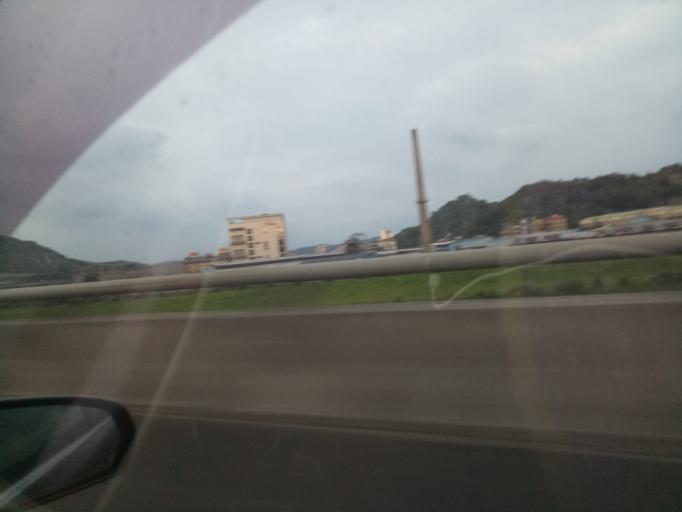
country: TW
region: Taiwan
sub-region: Keelung
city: Keelung
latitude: 25.0939
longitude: 121.6972
